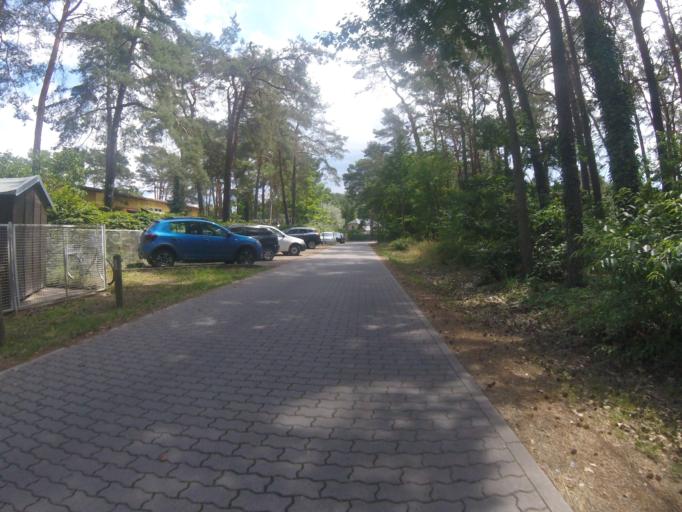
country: DE
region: Brandenburg
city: Bestensee
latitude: 52.2485
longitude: 13.6389
